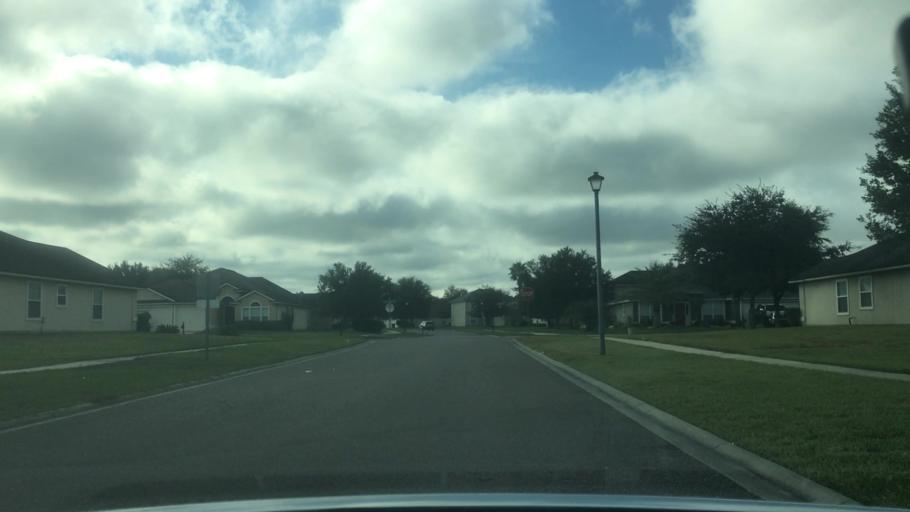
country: US
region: Florida
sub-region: Nassau County
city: Yulee
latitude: 30.4915
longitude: -81.5697
